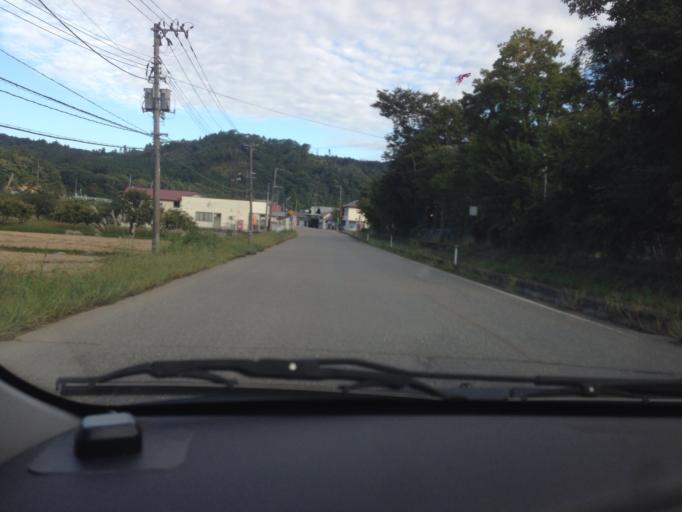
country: JP
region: Fukushima
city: Kitakata
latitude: 37.5756
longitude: 139.7631
